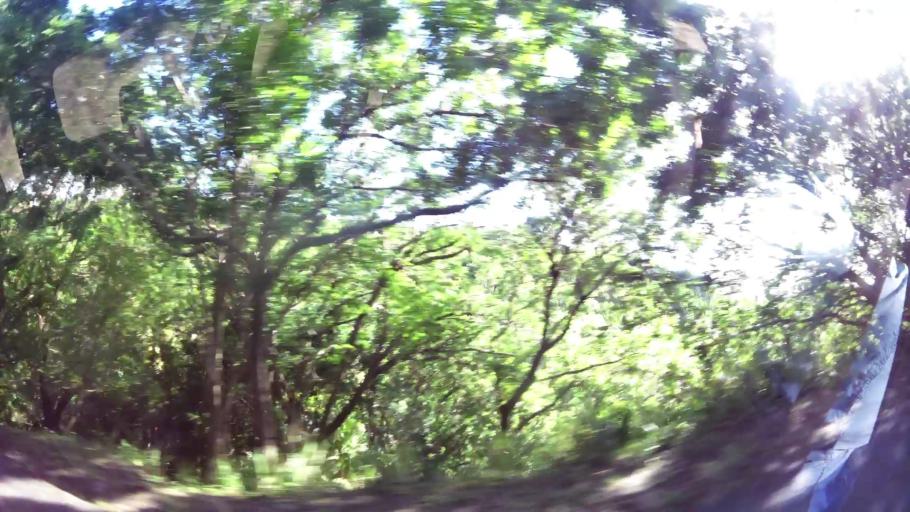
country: MS
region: Saint Peter
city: Saint Peters
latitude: 16.7486
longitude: -62.2184
